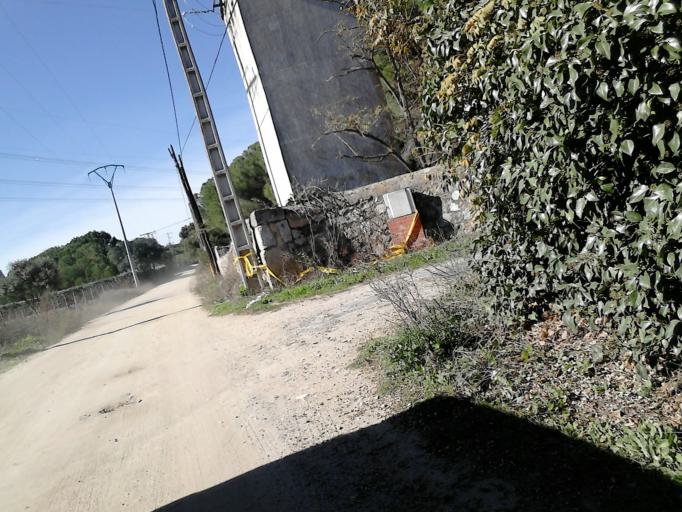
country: ES
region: Madrid
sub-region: Provincia de Madrid
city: Galapagar
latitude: 40.5736
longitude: -3.9788
